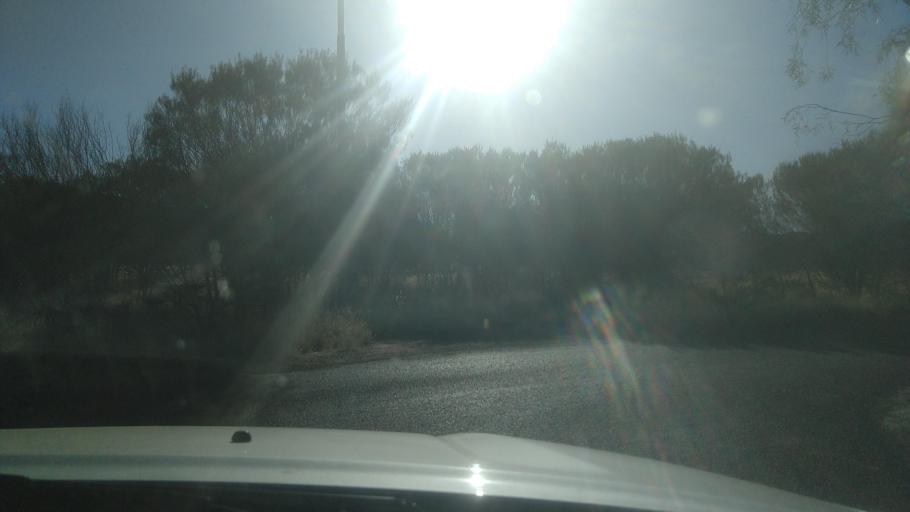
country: AU
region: Northern Territory
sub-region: Alice Springs
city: Alice Springs
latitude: -23.7048
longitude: 133.8316
